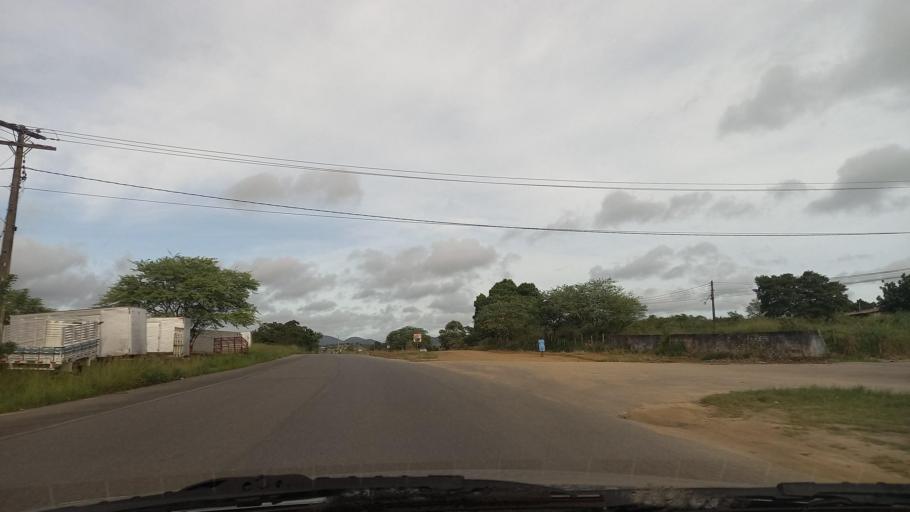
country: BR
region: Pernambuco
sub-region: Pombos
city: Pombos
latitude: -8.1257
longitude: -35.3473
